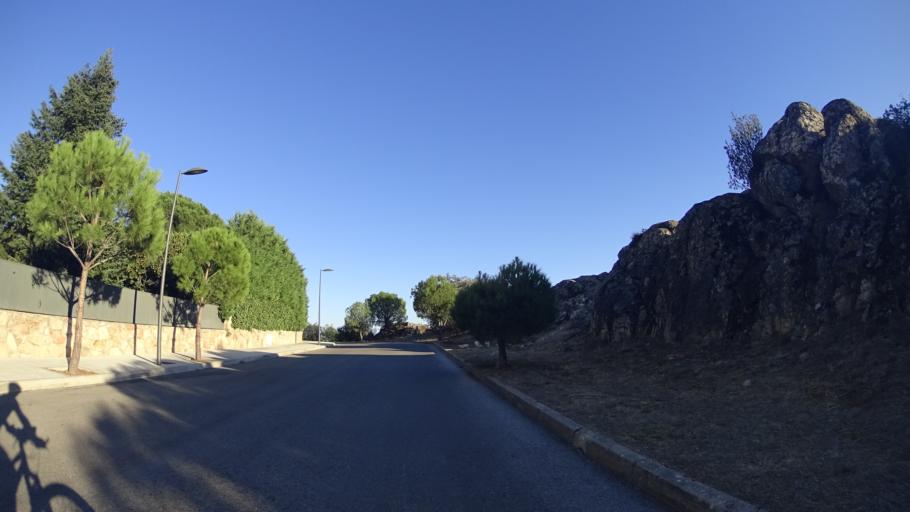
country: ES
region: Madrid
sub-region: Provincia de Madrid
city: Torrelodones
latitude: 40.5710
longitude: -3.9352
